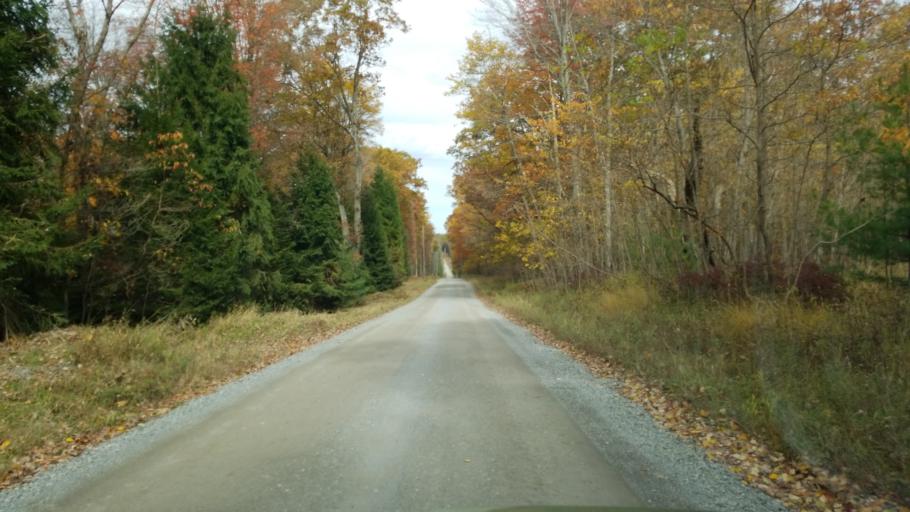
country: US
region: Pennsylvania
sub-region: Clearfield County
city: Clearfield
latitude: 41.1750
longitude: -78.4440
